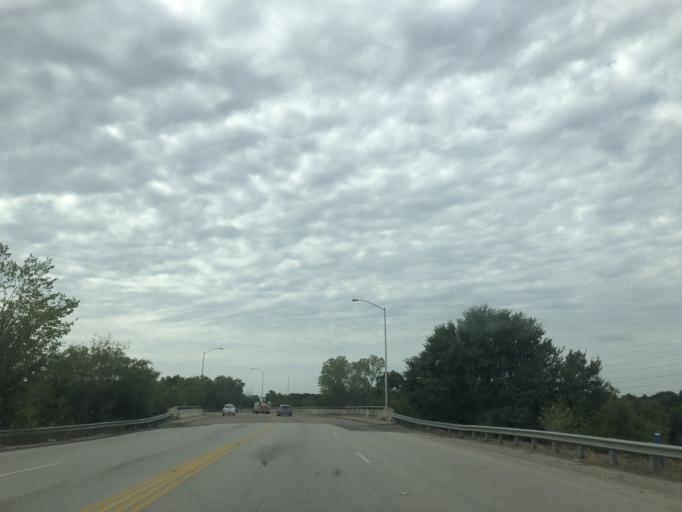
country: US
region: Texas
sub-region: Tarrant County
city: Richland Hills
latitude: 32.7834
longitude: -97.2213
